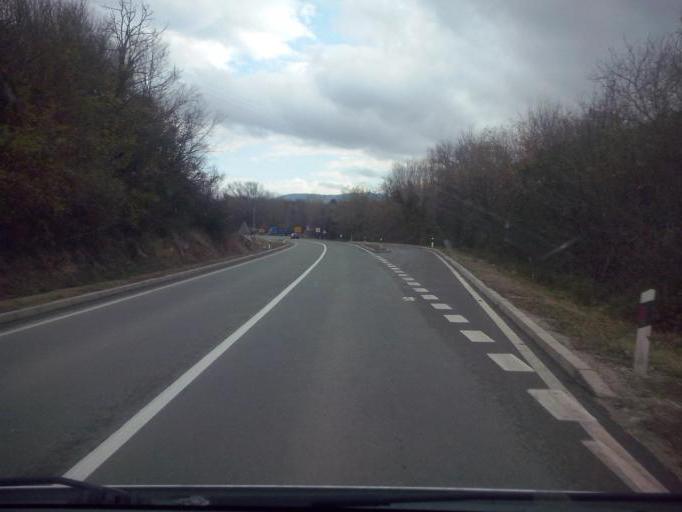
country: RS
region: Central Serbia
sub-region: Pomoravski Okrug
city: Paracin
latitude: 43.8600
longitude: 21.5305
